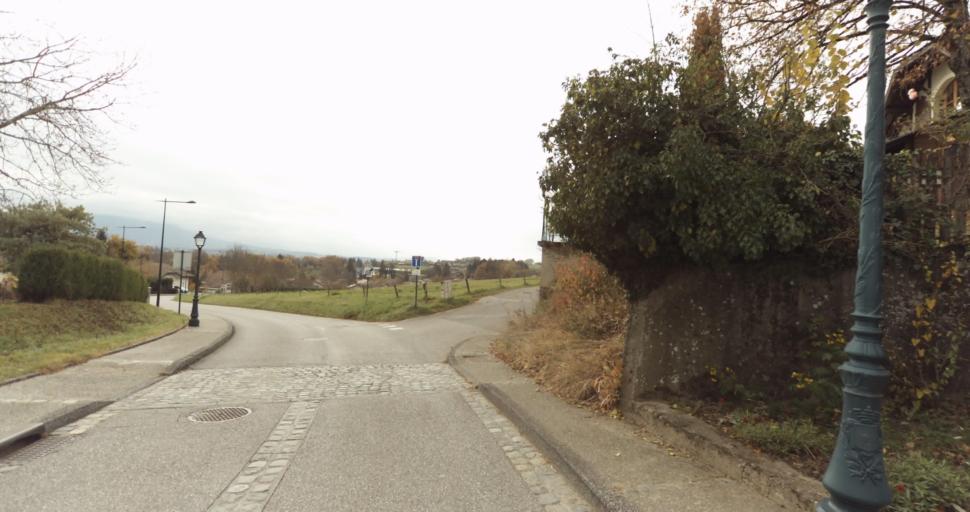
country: FR
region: Rhone-Alpes
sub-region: Departement de la Haute-Savoie
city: Pringy
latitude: 45.9534
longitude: 6.1110
